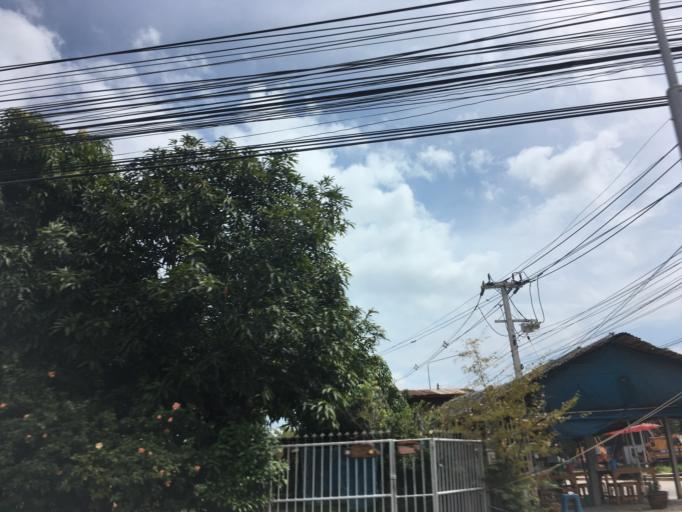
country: TH
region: Chachoengsao
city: Bang Khla
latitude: 13.7179
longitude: 101.2078
